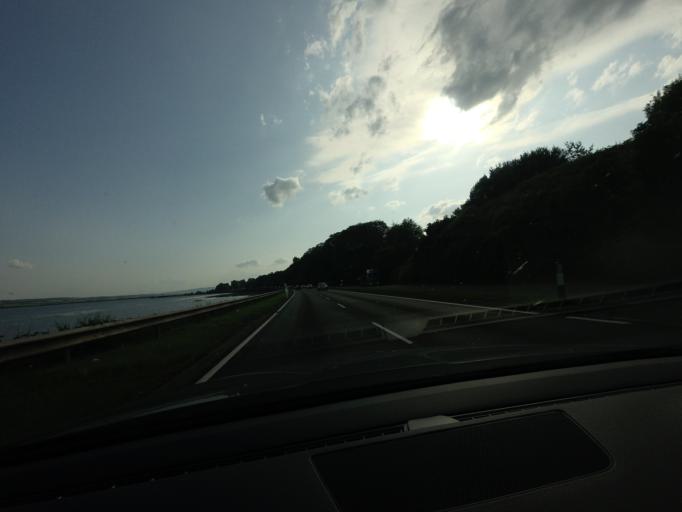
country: GB
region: Scotland
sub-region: Highland
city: Evanton
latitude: 57.6361
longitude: -4.3578
